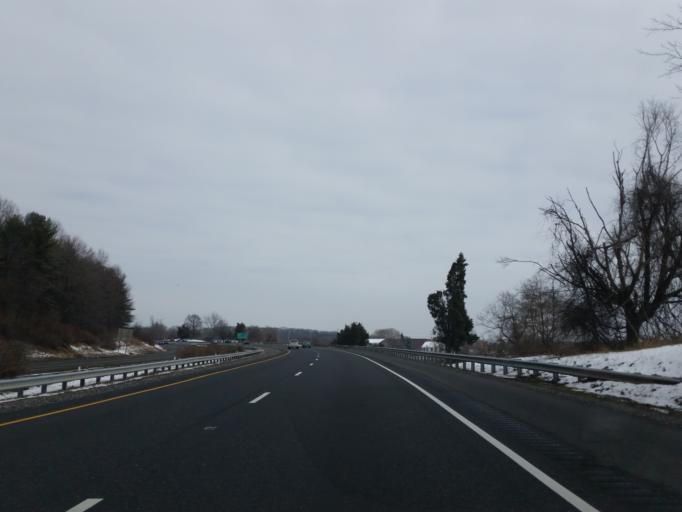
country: US
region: Maryland
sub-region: Baltimore County
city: Hunt Valley
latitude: 39.5962
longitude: -76.6661
